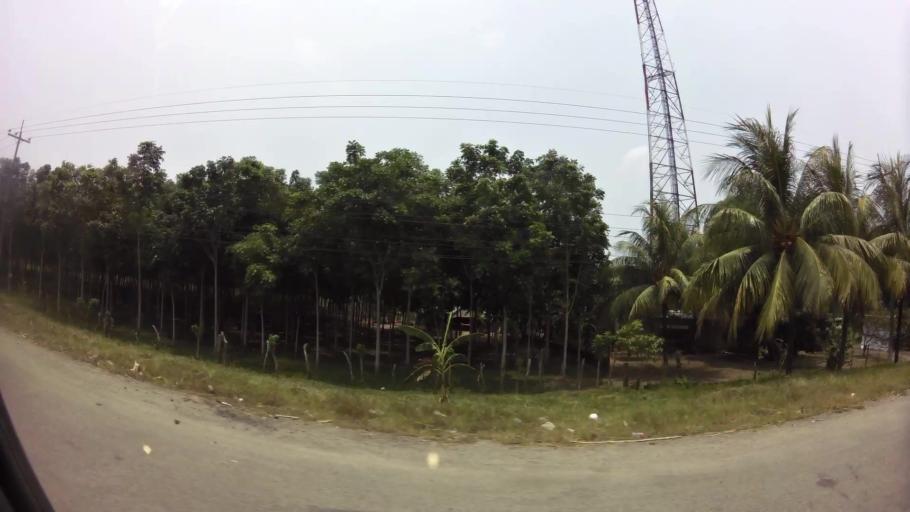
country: HN
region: Yoro
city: El Progreso
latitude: 15.4118
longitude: -87.8505
